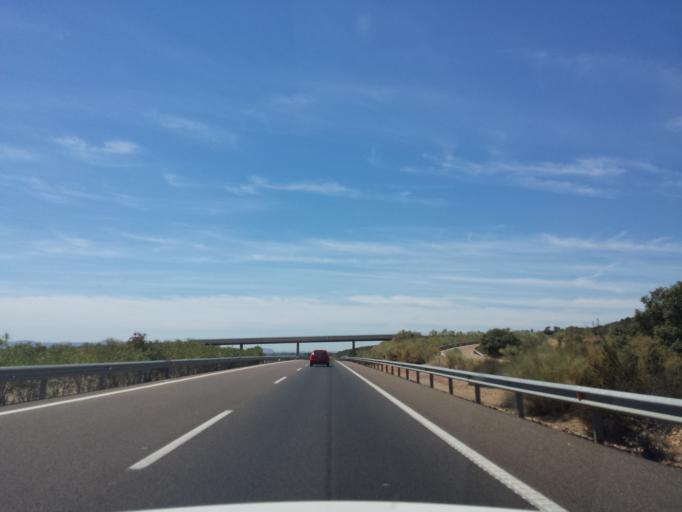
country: ES
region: Extremadura
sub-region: Provincia de Badajoz
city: San Pedro de Merida
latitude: 38.9727
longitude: -6.1488
